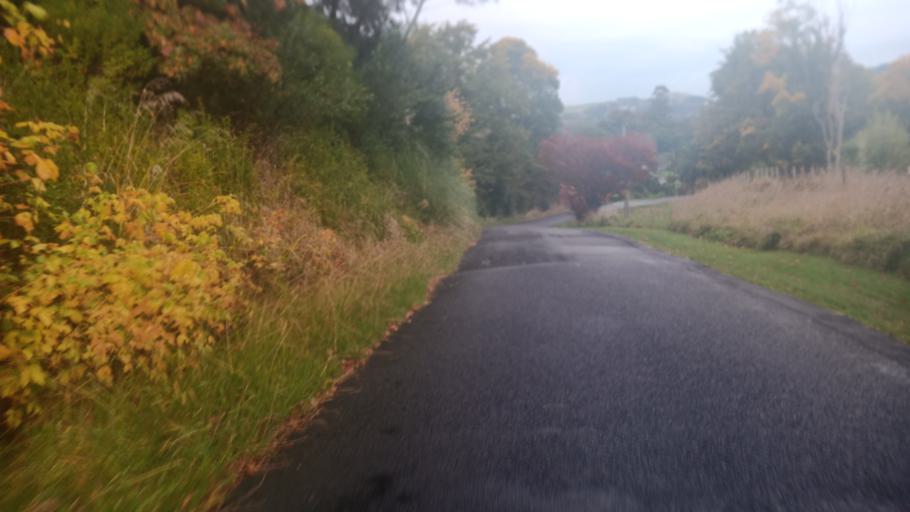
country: NZ
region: Gisborne
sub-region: Gisborne District
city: Gisborne
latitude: -38.6611
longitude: 178.0418
